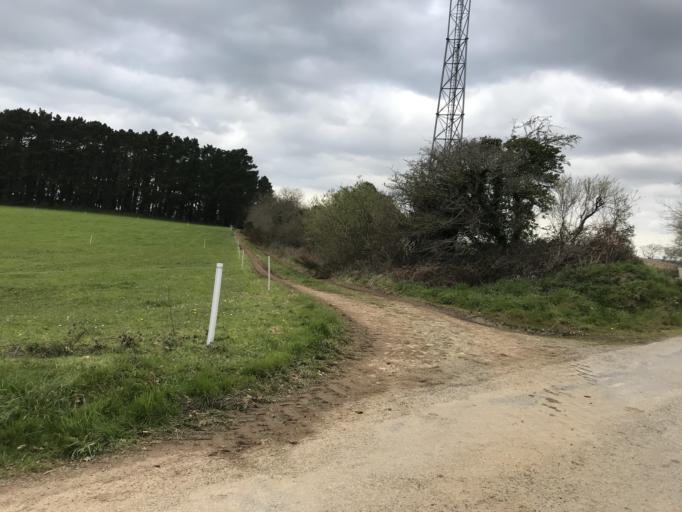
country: FR
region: Brittany
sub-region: Departement du Finistere
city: Hopital-Camfrout
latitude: 48.3201
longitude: -4.2411
